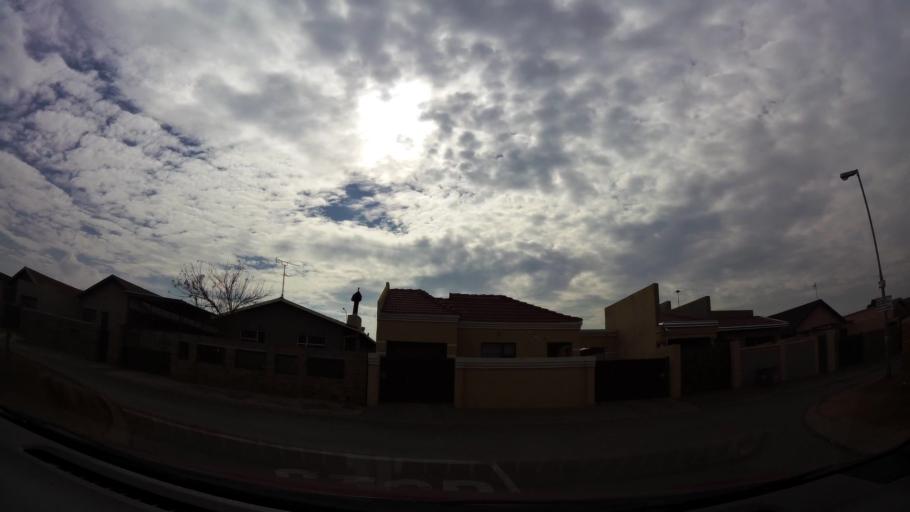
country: ZA
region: Gauteng
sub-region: City of Johannesburg Metropolitan Municipality
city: Soweto
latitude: -26.2714
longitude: 27.8295
